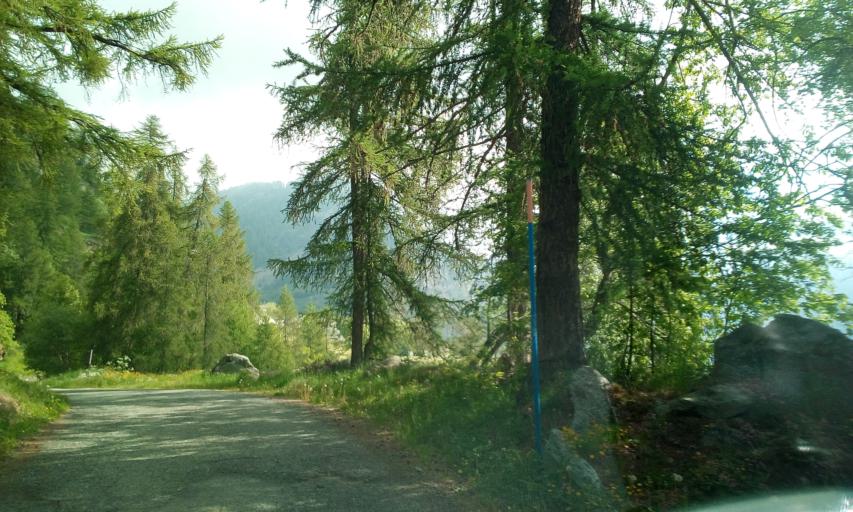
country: IT
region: Aosta Valley
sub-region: Valle d'Aosta
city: Antey-Saint-Andre
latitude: 45.8149
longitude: 7.5786
